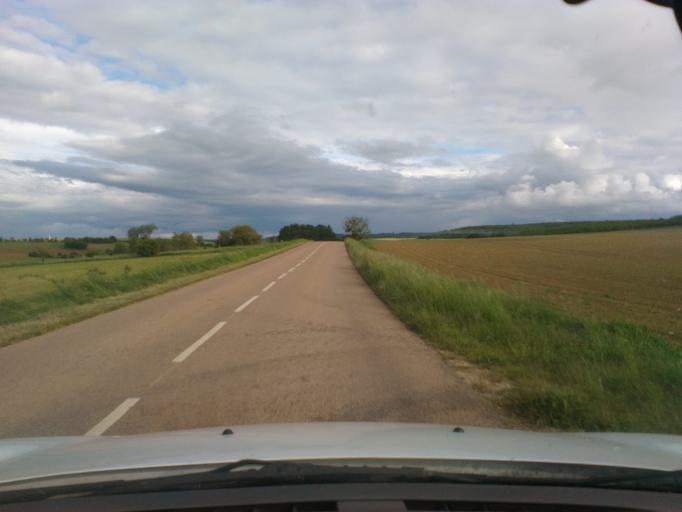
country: FR
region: Lorraine
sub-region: Departement des Vosges
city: Mirecourt
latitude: 48.3245
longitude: 6.0432
